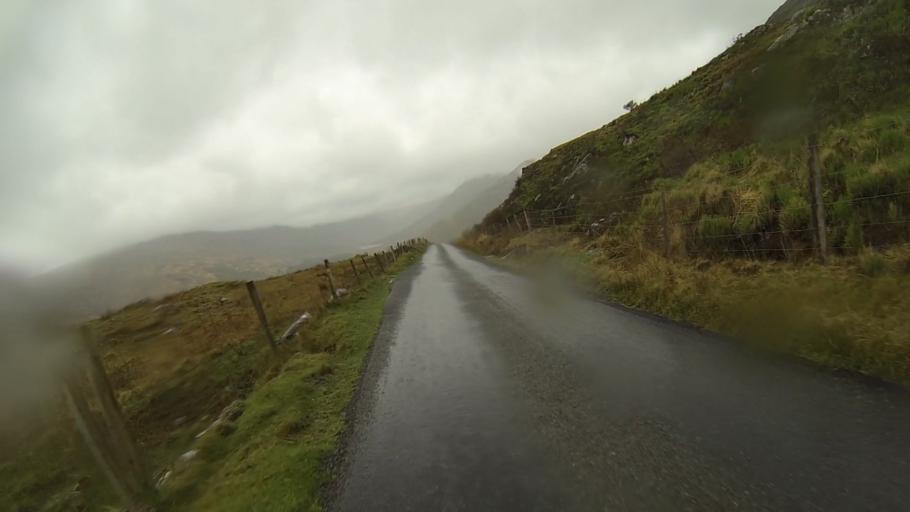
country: IE
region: Munster
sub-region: Ciarrai
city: Kenmare
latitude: 51.9904
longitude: -9.6468
